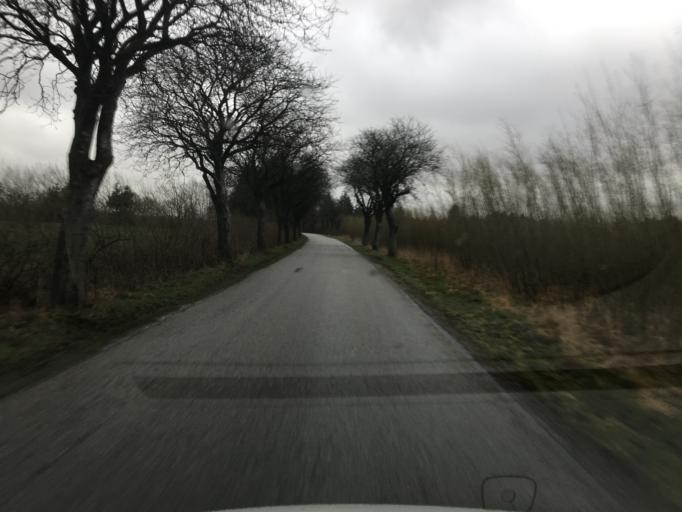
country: DK
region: South Denmark
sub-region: Aabenraa Kommune
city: Padborg
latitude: 54.8996
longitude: 9.3415
